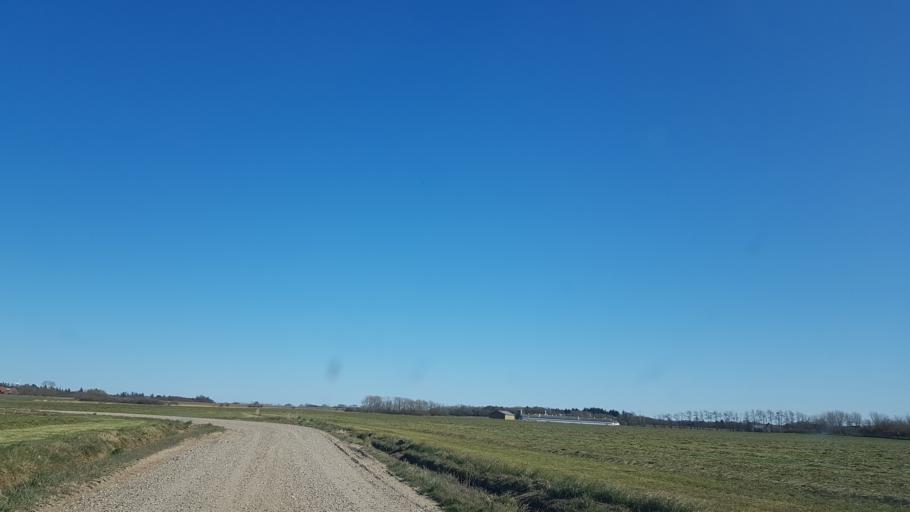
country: DK
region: South Denmark
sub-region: Tonder Kommune
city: Sherrebek
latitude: 55.2402
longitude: 8.7112
